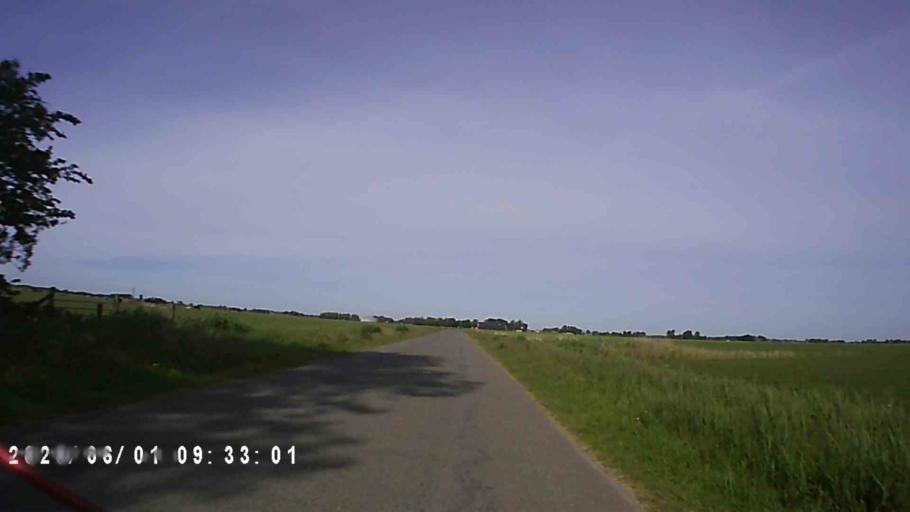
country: NL
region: Friesland
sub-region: Gemeente Leeuwarderadeel
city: Stiens
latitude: 53.2620
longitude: 5.7240
